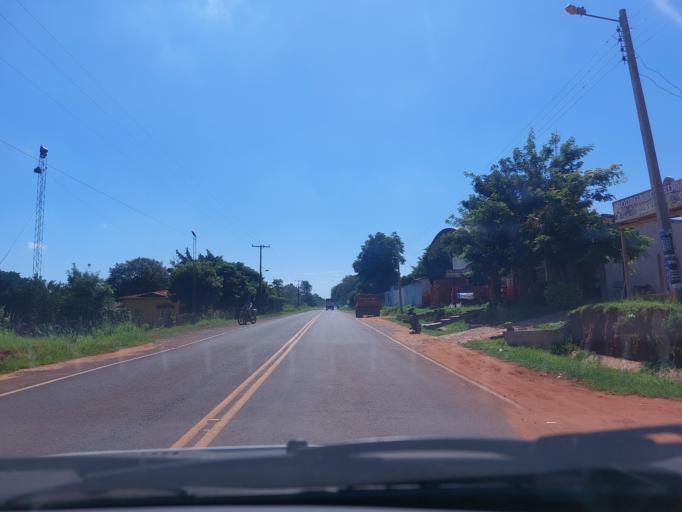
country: PY
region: San Pedro
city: Guayaybi
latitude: -24.5933
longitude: -56.5196
